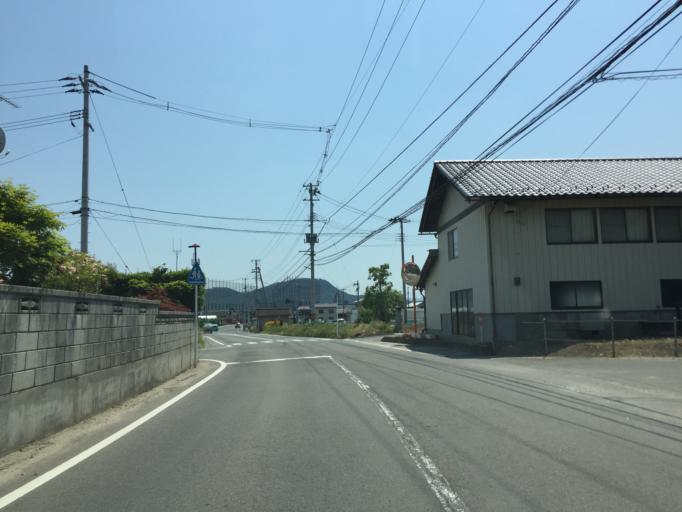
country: JP
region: Fukushima
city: Fukushima-shi
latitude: 37.7990
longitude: 140.4725
